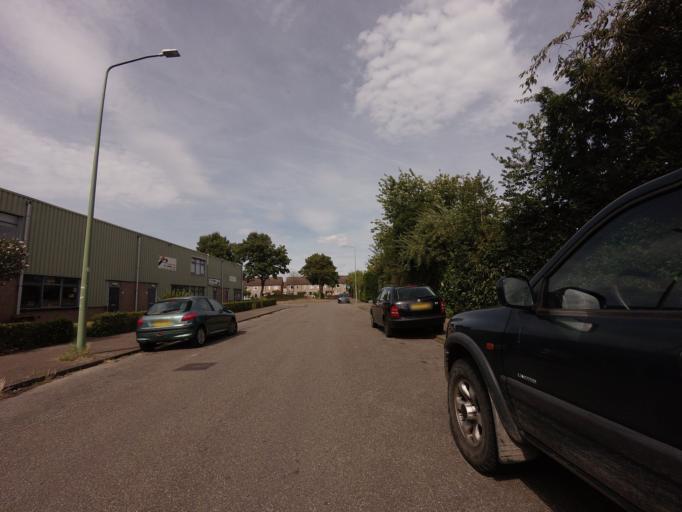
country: NL
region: Utrecht
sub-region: Gemeente Zeist
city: Zeist
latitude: 52.0886
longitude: 5.2126
